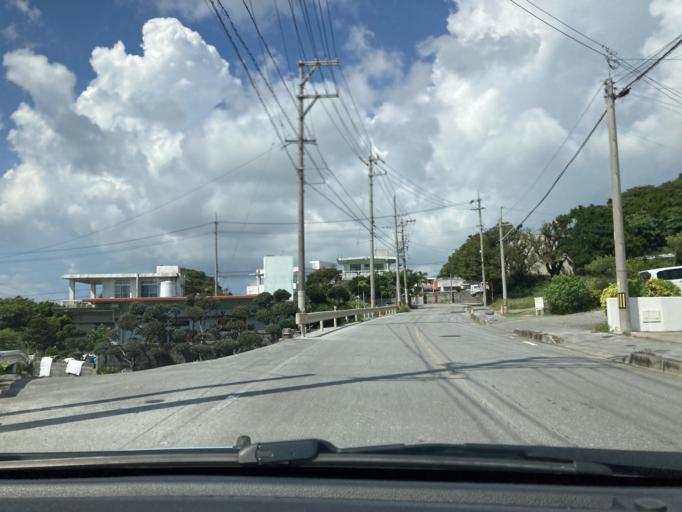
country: JP
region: Okinawa
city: Tomigusuku
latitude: 26.1395
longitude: 127.7887
